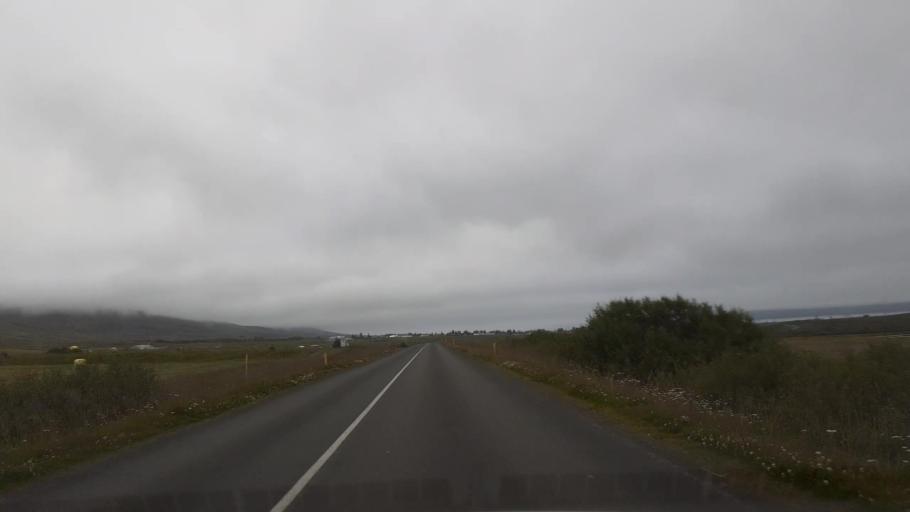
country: IS
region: Northeast
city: Dalvik
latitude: 65.9515
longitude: -18.5534
